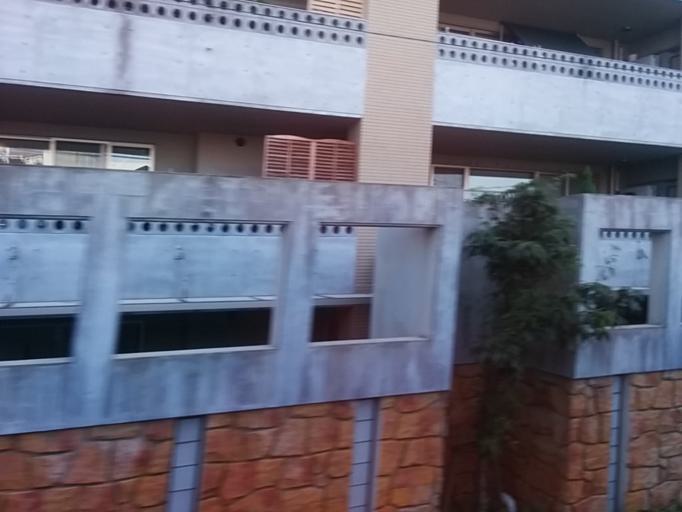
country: JP
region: Nara
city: Nara-shi
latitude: 34.6978
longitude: 135.7806
